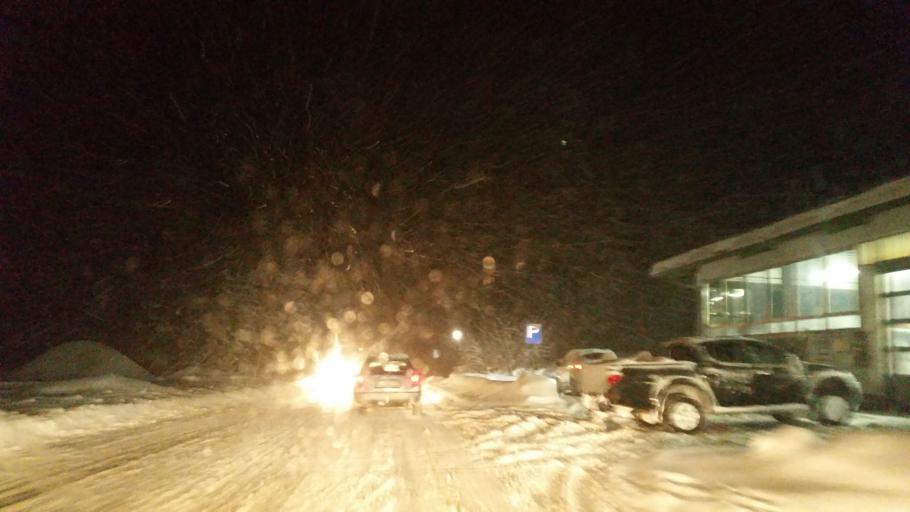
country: AT
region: Salzburg
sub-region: Politischer Bezirk Hallein
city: Abtenau
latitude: 47.5235
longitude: 13.4312
